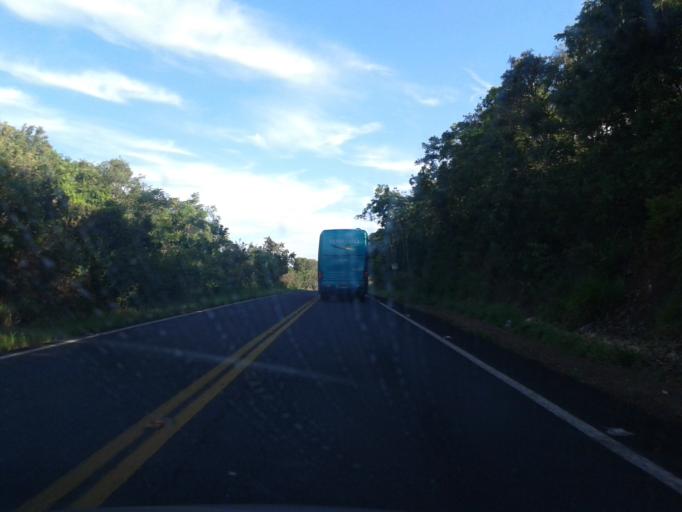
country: BR
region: Minas Gerais
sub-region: Tupaciguara
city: Tupaciguara
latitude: -18.2989
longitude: -48.5631
